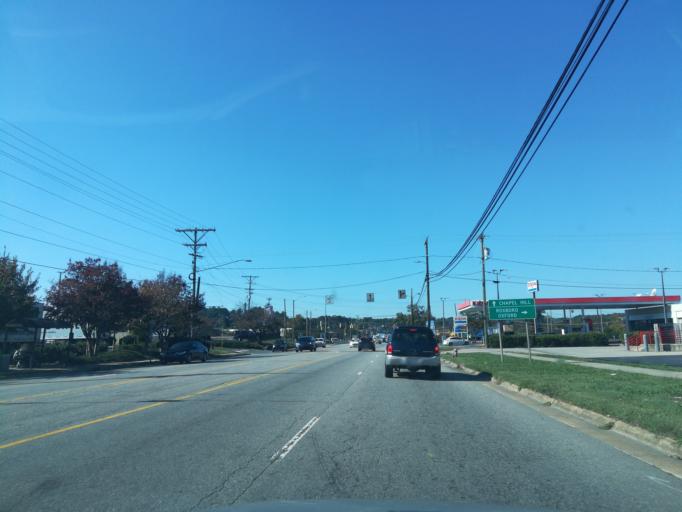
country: US
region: North Carolina
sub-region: Durham County
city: Durham
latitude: 36.0198
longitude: -78.9472
